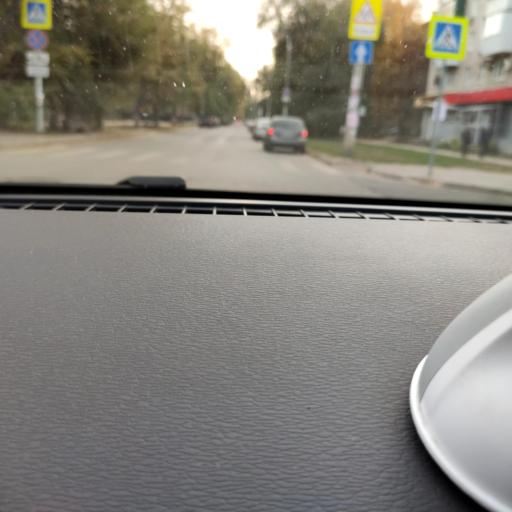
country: RU
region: Samara
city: Petra-Dubrava
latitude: 53.2351
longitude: 50.2820
